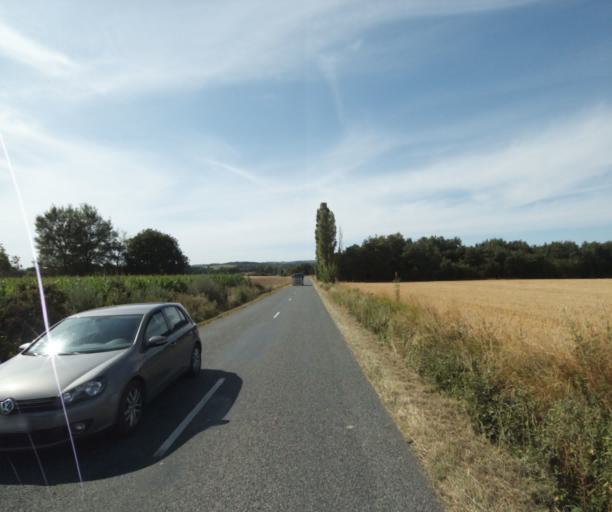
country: FR
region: Midi-Pyrenees
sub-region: Departement du Tarn
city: Soual
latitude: 43.5127
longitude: 2.0833
